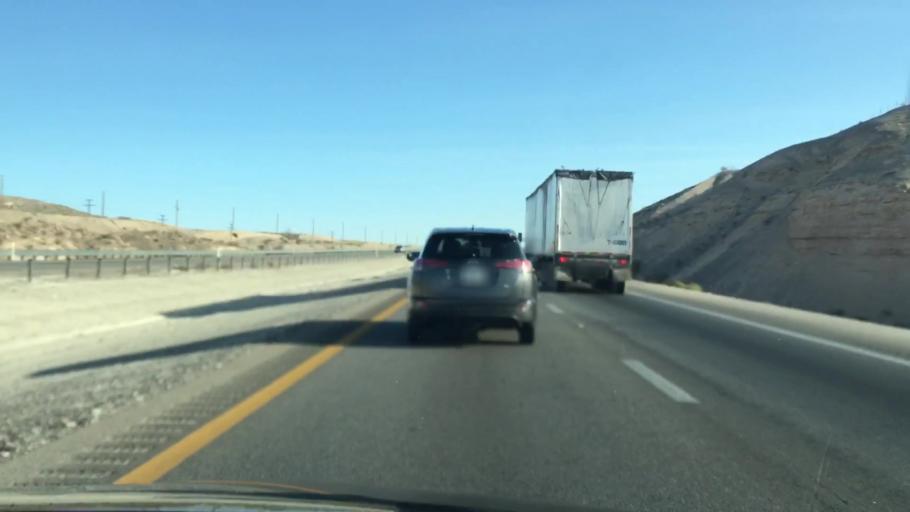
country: US
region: Nevada
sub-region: Clark County
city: Nellis Air Force Base
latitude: 36.3174
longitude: -114.9404
